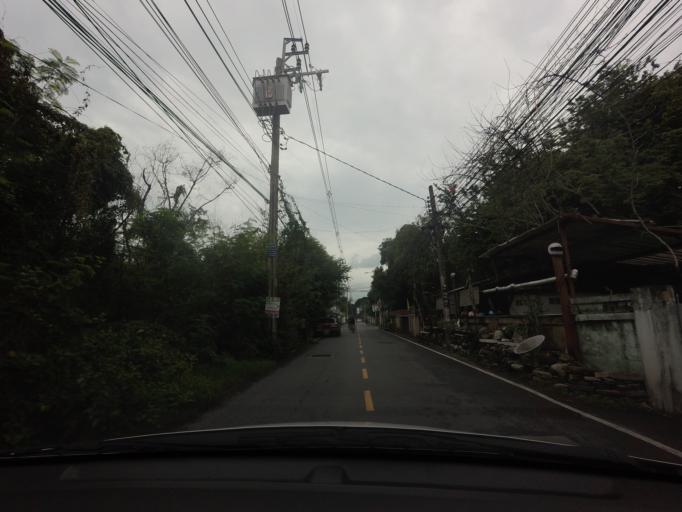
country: TH
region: Nonthaburi
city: Pak Kret
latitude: 13.9018
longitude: 100.5126
